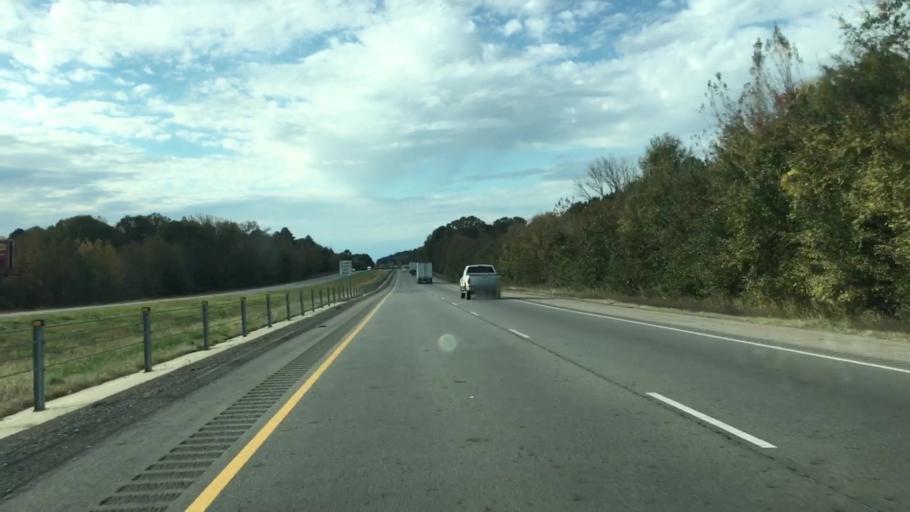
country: US
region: Arkansas
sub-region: Pope County
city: Pottsville
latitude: 35.2528
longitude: -93.0426
